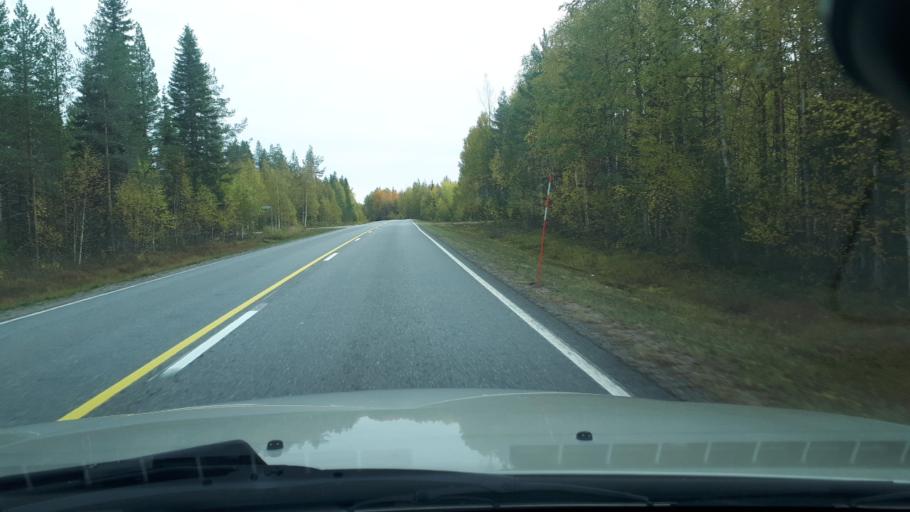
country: FI
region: Lapland
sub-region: Rovaniemi
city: Ranua
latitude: 66.0096
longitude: 26.2872
